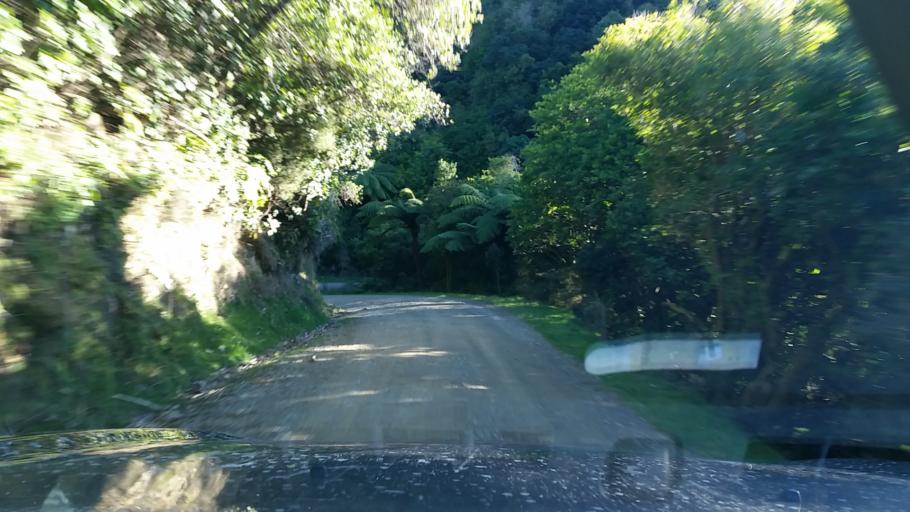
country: NZ
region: Marlborough
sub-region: Marlborough District
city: Picton
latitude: -41.0267
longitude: 174.1501
